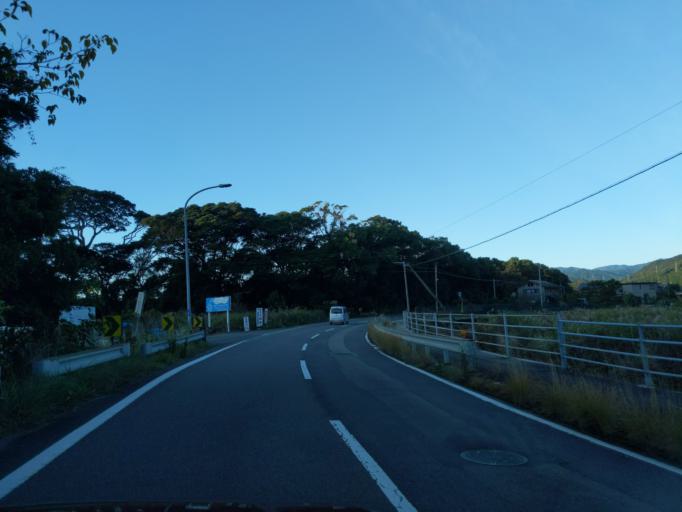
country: JP
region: Kochi
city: Muroto-misakicho
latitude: 33.5833
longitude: 134.3299
